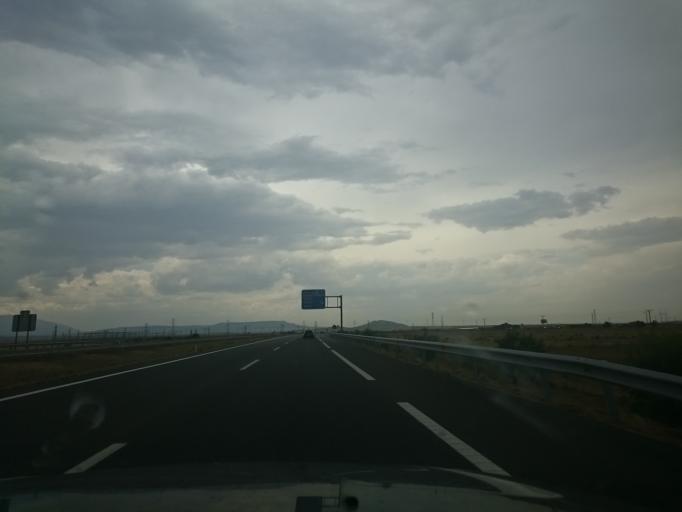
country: ES
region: Aragon
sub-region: Provincia de Zaragoza
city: Gallur
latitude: 41.8469
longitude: -1.3633
